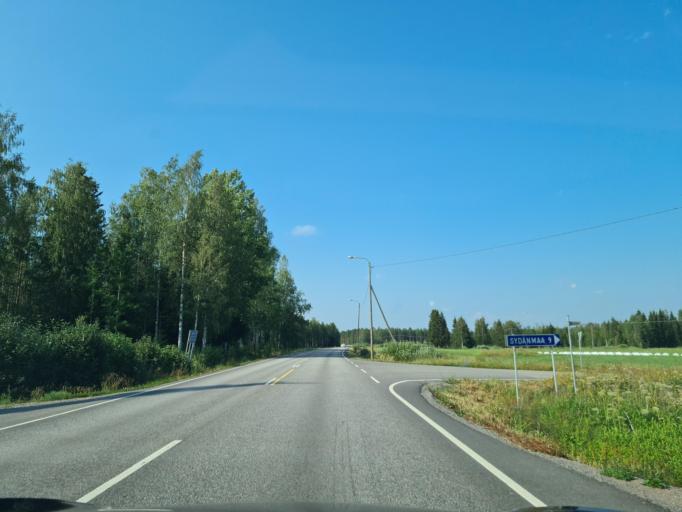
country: FI
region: Satakunta
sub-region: Pohjois-Satakunta
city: Kankaanpaeae
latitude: 61.9514
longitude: 22.5132
